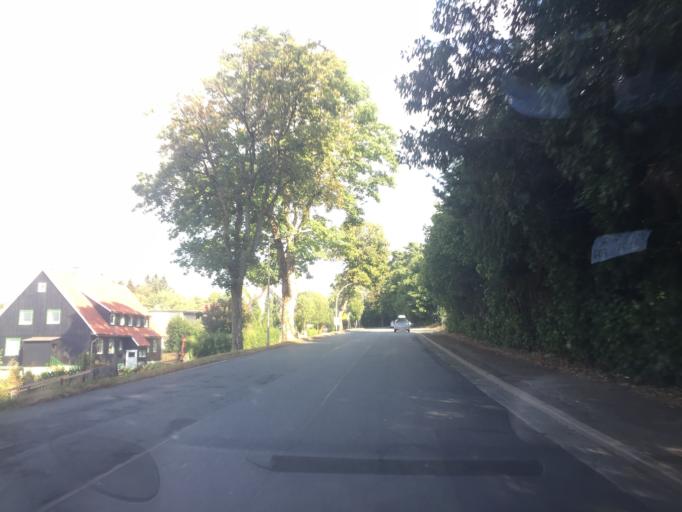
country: DE
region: Lower Saxony
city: Braunlage
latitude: 51.7161
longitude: 10.6183
